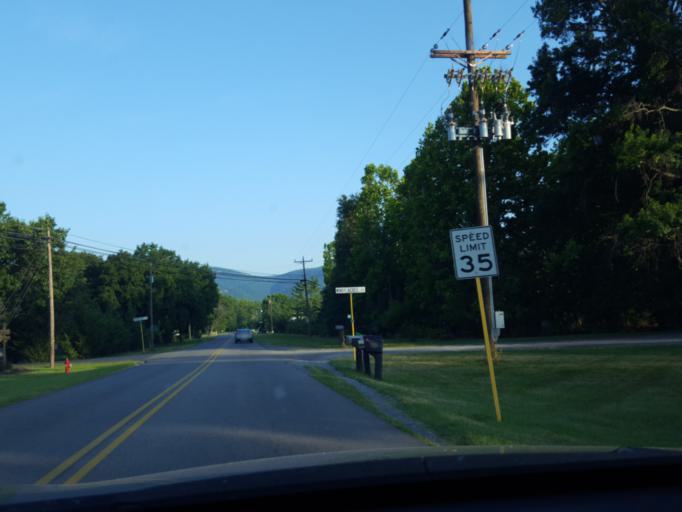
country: US
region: Virginia
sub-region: Augusta County
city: Lyndhurst
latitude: 37.9875
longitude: -78.9565
